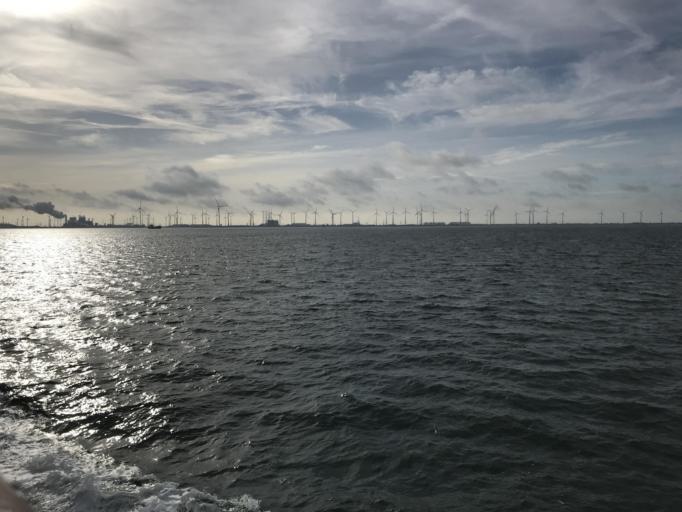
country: DE
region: Lower Saxony
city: Borkum
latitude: 53.4956
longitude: 6.8218
